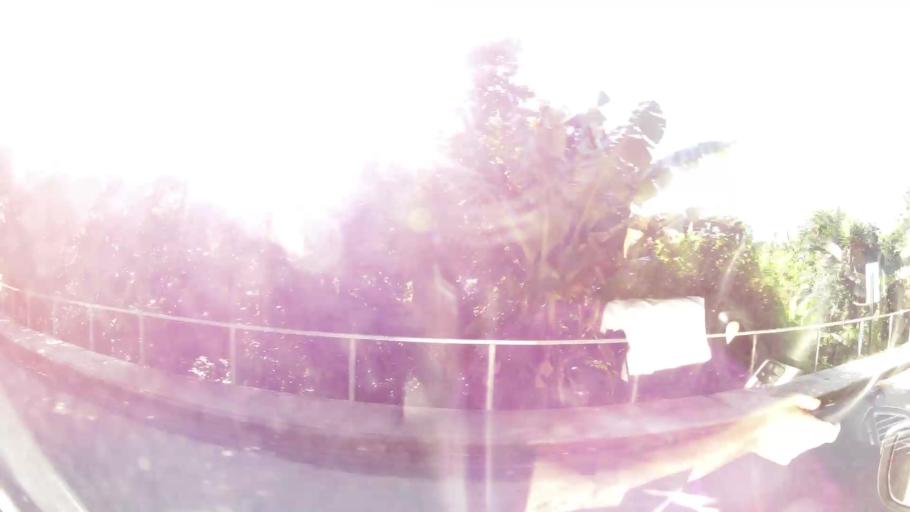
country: CR
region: Guanacaste
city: Juntas
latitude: 10.3162
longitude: -84.8246
